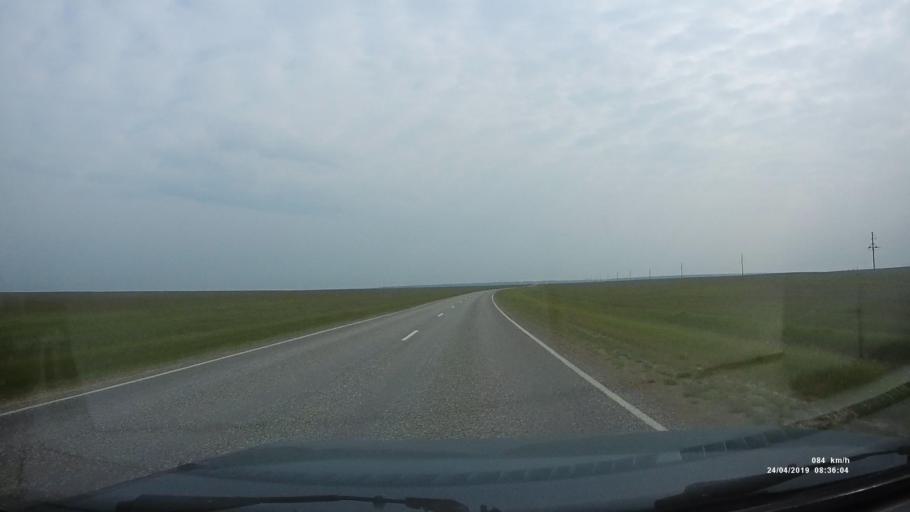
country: RU
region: Kalmykiya
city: Arshan'
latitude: 46.2024
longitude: 43.9284
